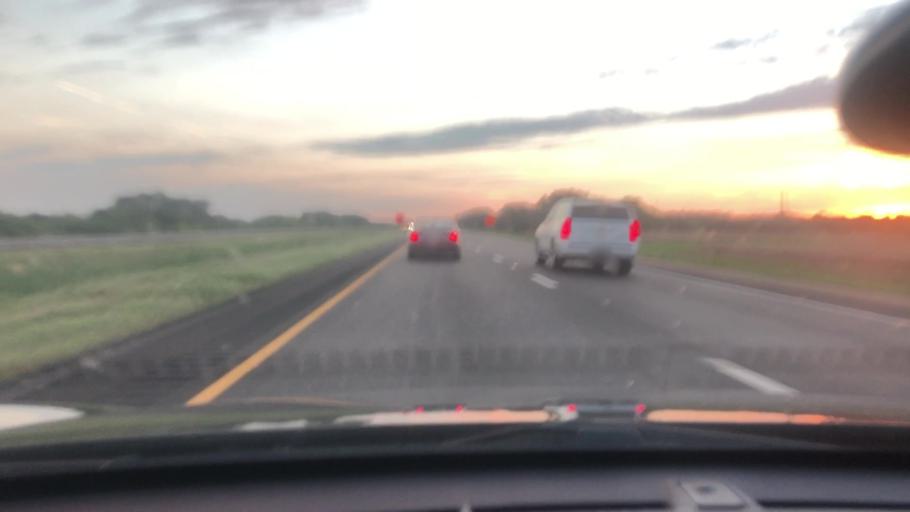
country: US
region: Texas
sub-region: Victoria County
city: Inez
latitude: 28.9207
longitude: -96.7597
